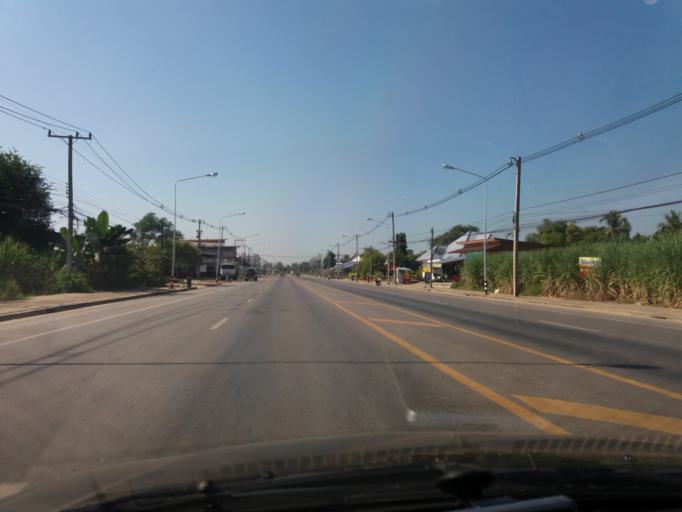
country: TH
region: Kamphaeng Phet
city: Khlong Khlung
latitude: 16.2245
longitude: 99.7299
